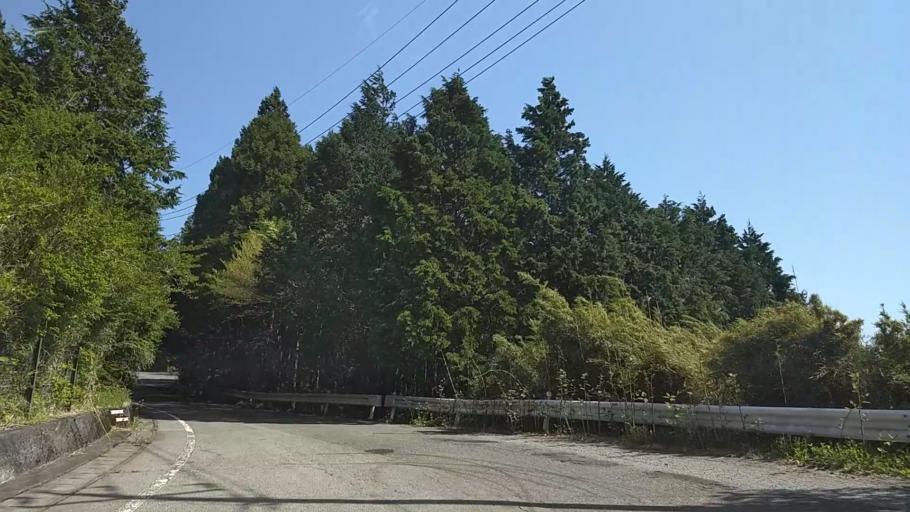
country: JP
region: Shizuoka
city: Gotemba
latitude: 35.2729
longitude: 138.9587
